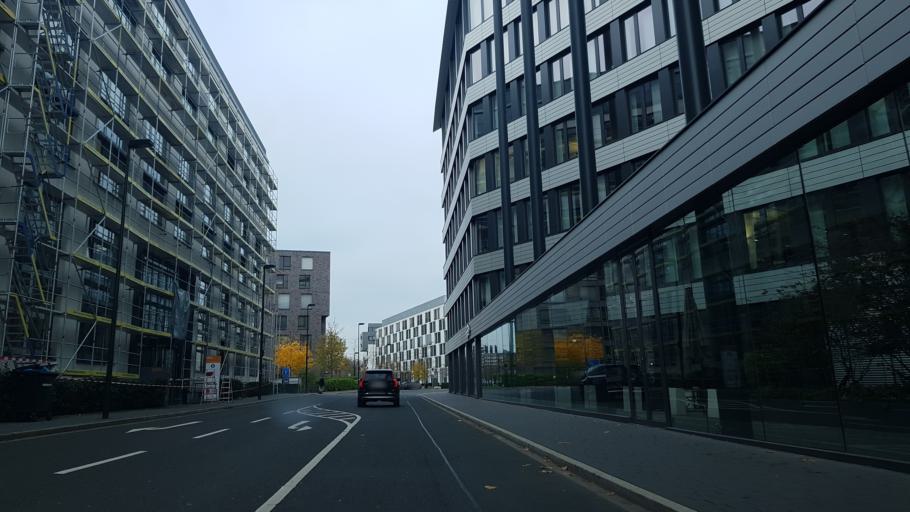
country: DE
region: North Rhine-Westphalia
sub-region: Regierungsbezirk Dusseldorf
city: Dusseldorf
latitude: 51.2532
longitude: 6.7861
